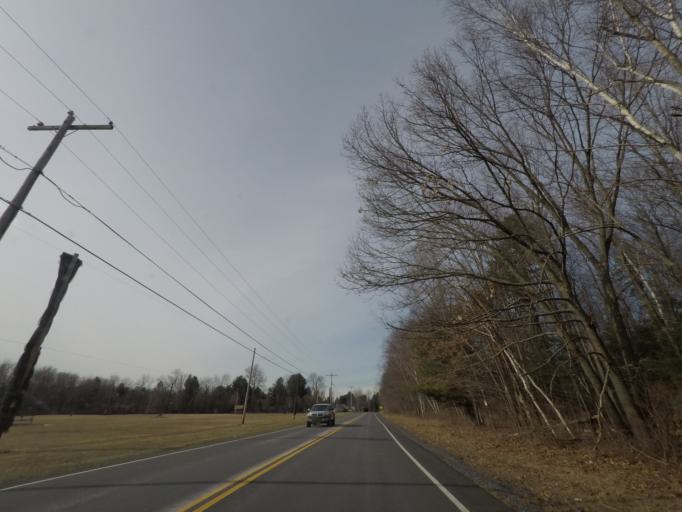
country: US
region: New York
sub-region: Columbia County
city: Valatie
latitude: 42.4020
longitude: -73.6706
